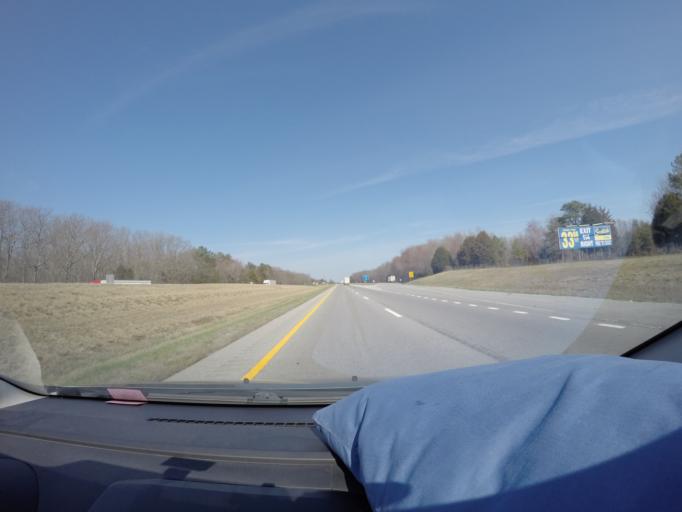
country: US
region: Tennessee
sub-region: Coffee County
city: Manchester
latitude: 35.3905
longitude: -85.9890
